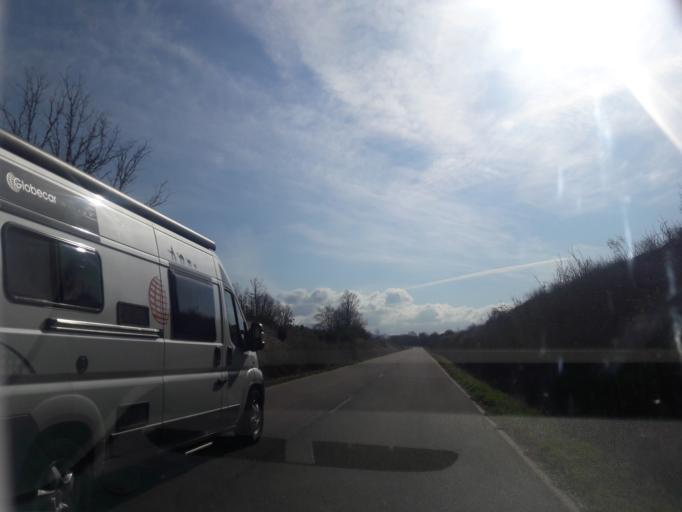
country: ES
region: Castille and Leon
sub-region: Provincia de Salamanca
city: Valdehijaderos
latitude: 40.4207
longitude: -5.8602
